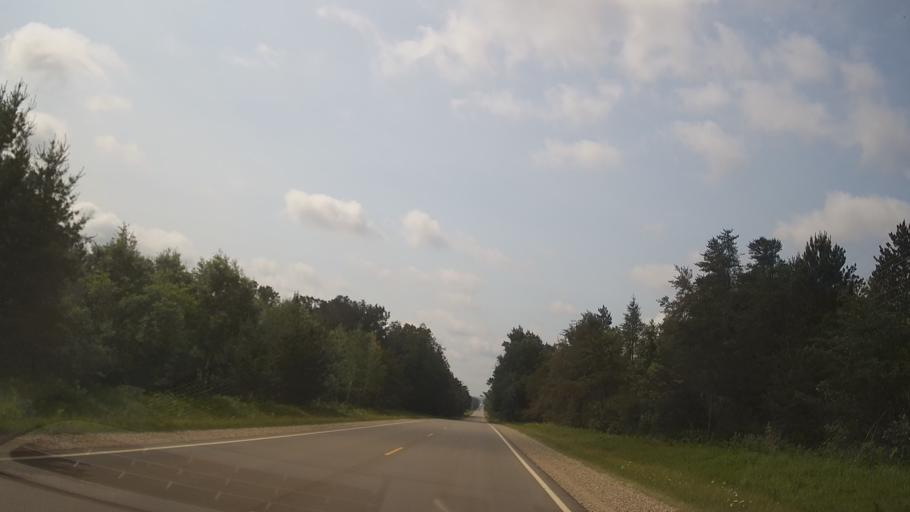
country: US
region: Michigan
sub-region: Roscommon County
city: Saint Helen
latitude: 44.3939
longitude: -84.4103
